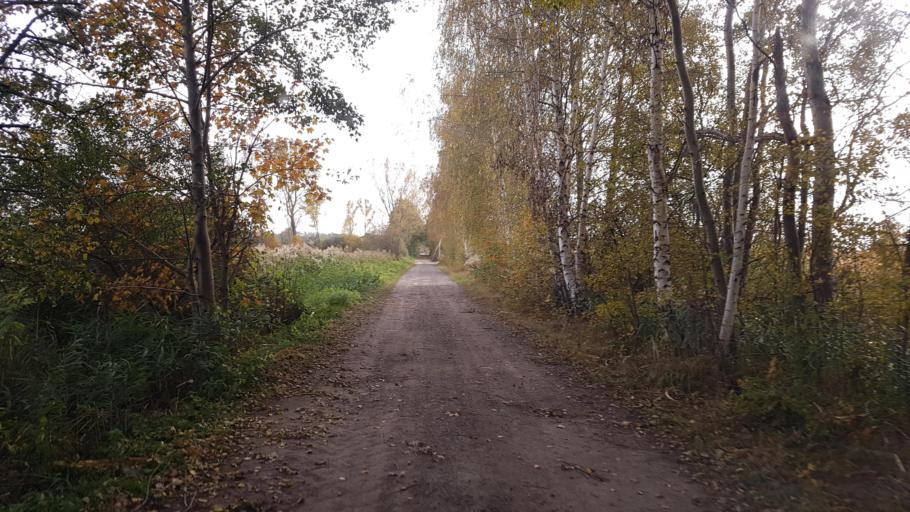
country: DE
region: Brandenburg
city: Schraden
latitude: 51.4497
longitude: 13.6918
